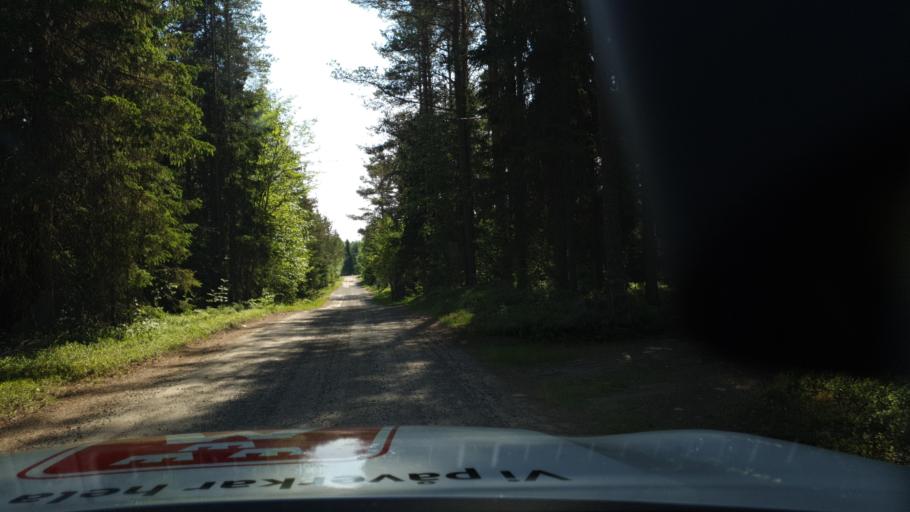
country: SE
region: Vaesterbotten
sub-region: Robertsfors Kommun
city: Robertsfors
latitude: 64.2260
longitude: 21.0651
